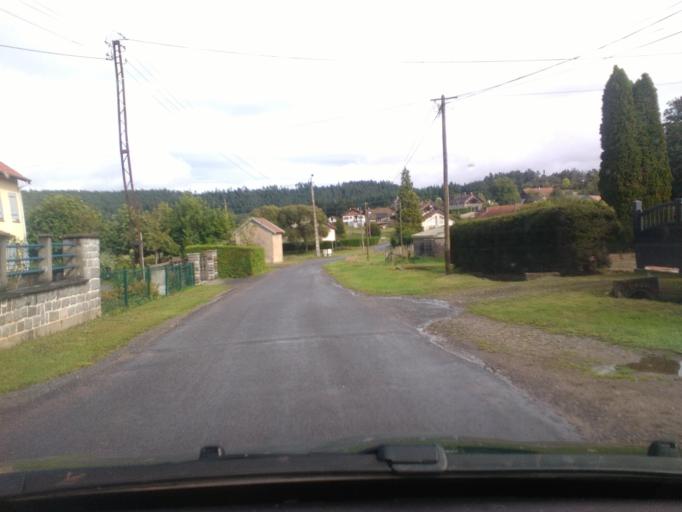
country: FR
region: Lorraine
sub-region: Departement des Vosges
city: Taintrux
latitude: 48.2318
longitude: 6.8894
